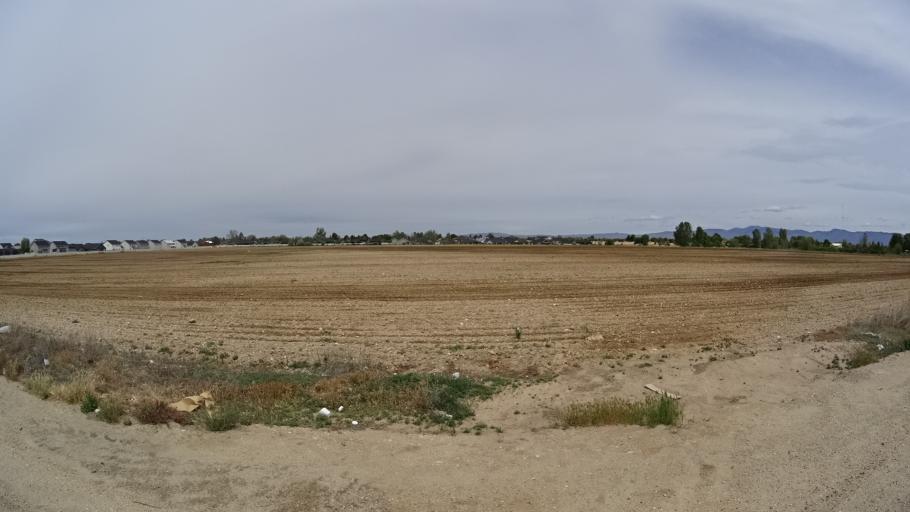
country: US
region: Idaho
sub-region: Ada County
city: Meridian
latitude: 43.5609
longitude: -116.3465
